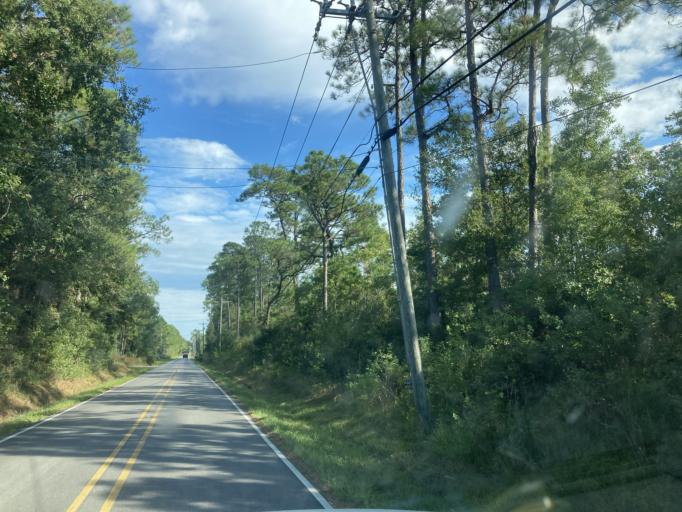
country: US
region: Mississippi
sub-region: Jackson County
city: Saint Martin
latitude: 30.4363
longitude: -88.8665
